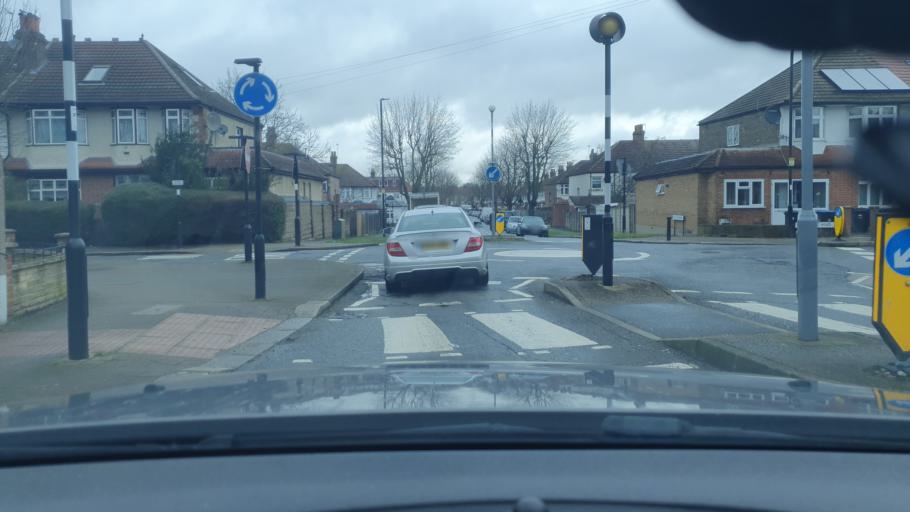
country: GB
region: England
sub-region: Greater London
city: Wood Green
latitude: 51.6109
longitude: -0.1024
